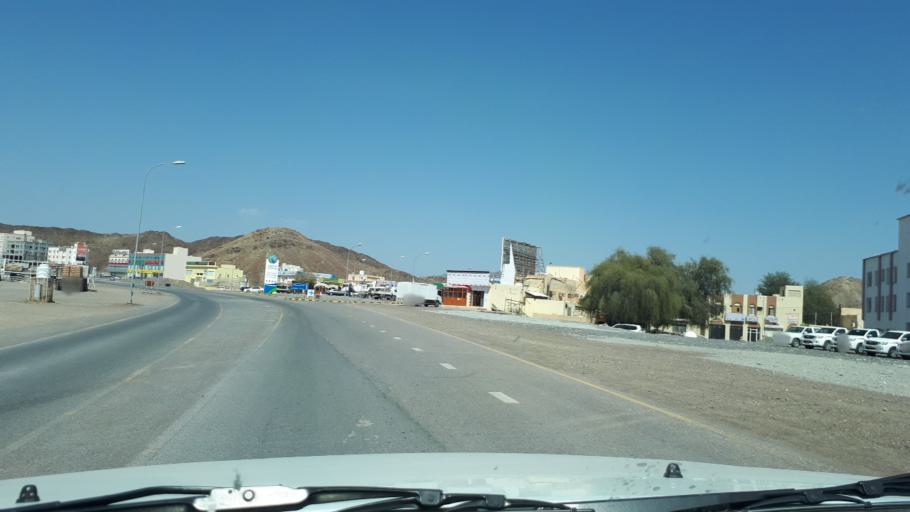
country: OM
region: Muhafazat ad Dakhiliyah
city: Bahla'
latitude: 22.9479
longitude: 57.2833
